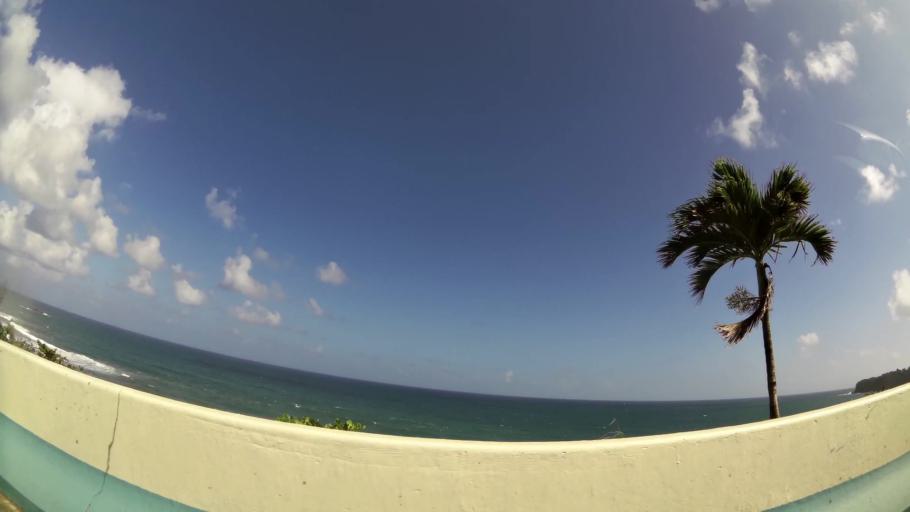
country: MQ
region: Martinique
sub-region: Martinique
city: Le Lorrain
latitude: 14.8355
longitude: -61.0597
